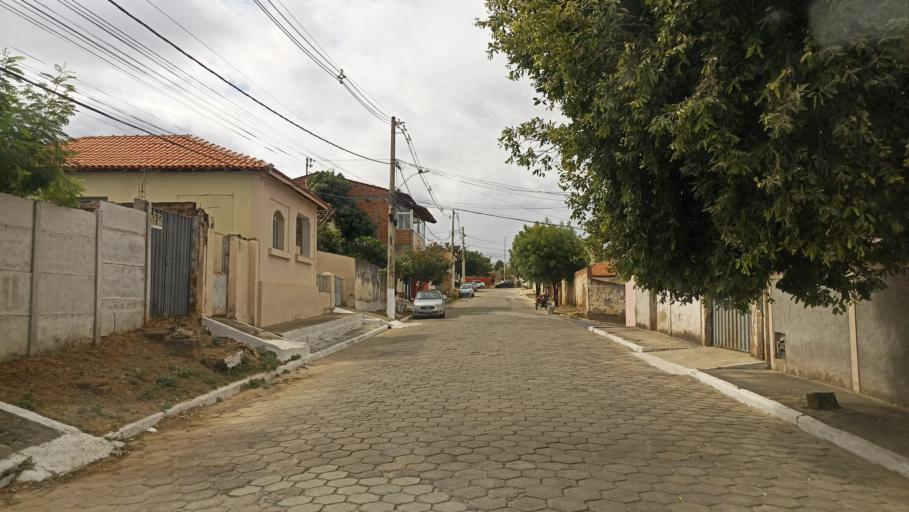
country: BR
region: Minas Gerais
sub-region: Aracuai
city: Aracuai
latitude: -16.8492
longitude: -42.0686
